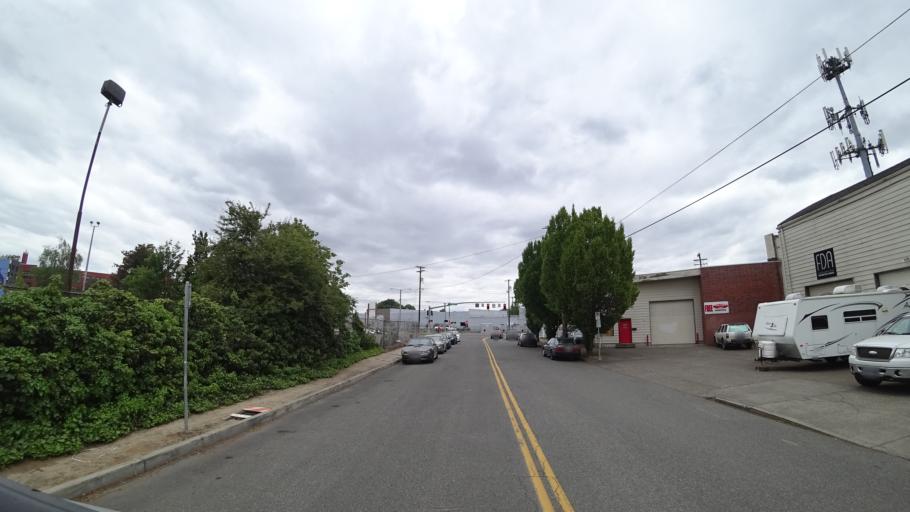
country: US
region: Oregon
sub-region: Multnomah County
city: Portland
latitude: 45.5030
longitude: -122.6554
